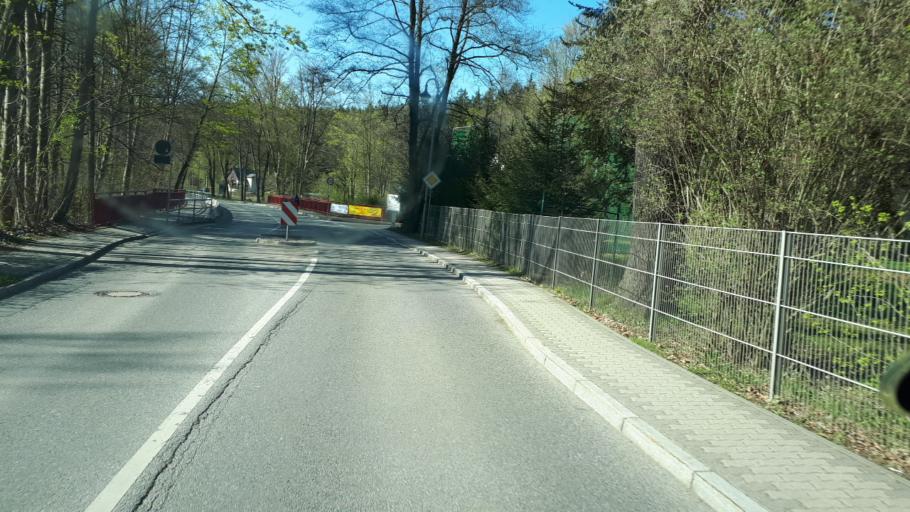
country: DE
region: Saxony
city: Chemnitz
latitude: 50.7823
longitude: 12.9722
